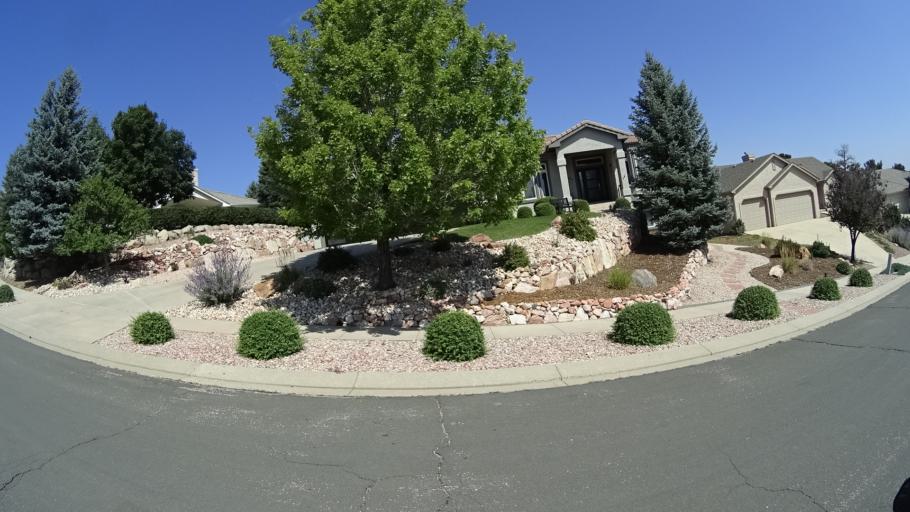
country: US
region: Colorado
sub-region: El Paso County
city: Manitou Springs
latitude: 38.9204
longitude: -104.8818
